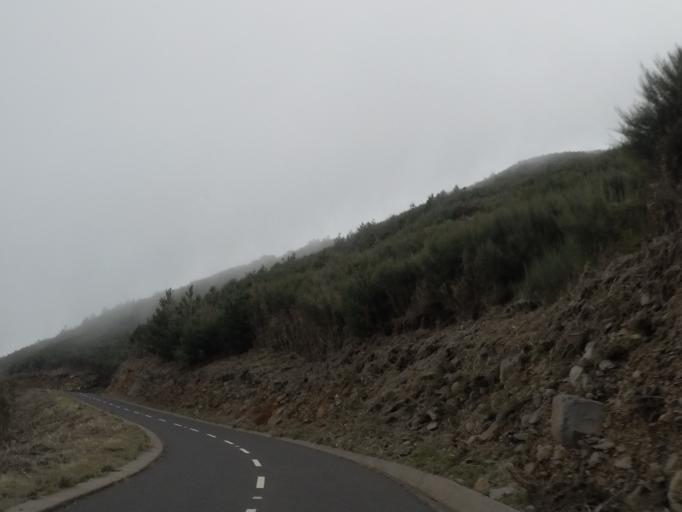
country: PT
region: Madeira
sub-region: Camara de Lobos
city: Curral das Freiras
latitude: 32.7268
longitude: -16.9398
